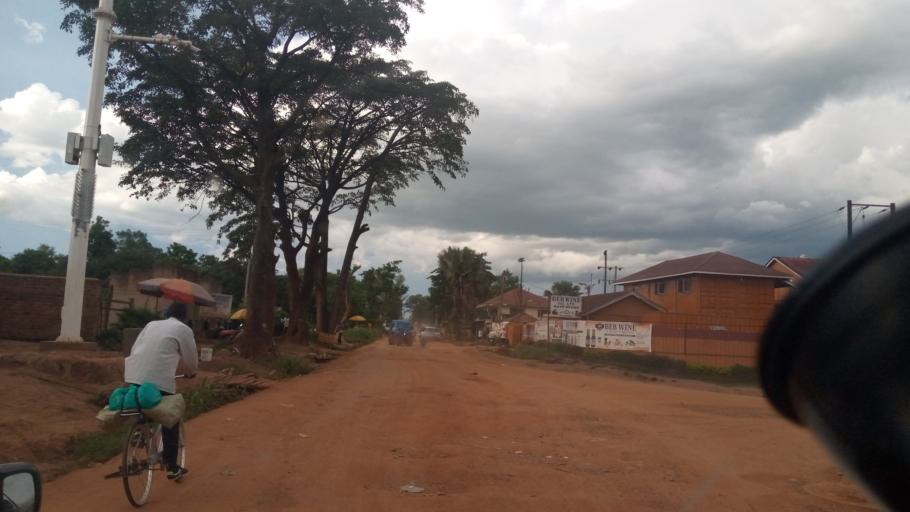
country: UG
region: Northern Region
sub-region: Lira District
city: Lira
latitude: 2.2545
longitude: 32.9047
